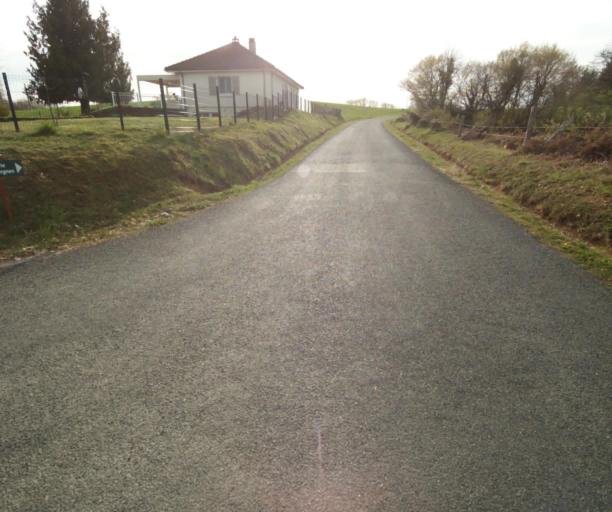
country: FR
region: Limousin
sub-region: Departement de la Correze
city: Naves
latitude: 45.3127
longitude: 1.7500
